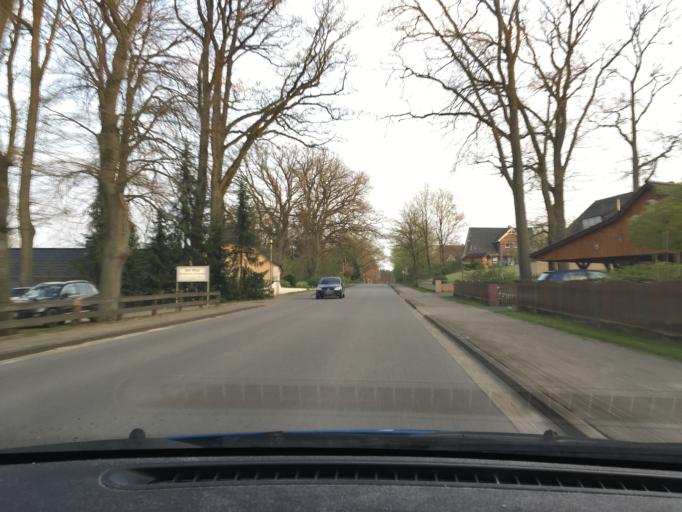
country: DE
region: Lower Saxony
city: Oldendorf
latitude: 53.1538
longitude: 10.2140
